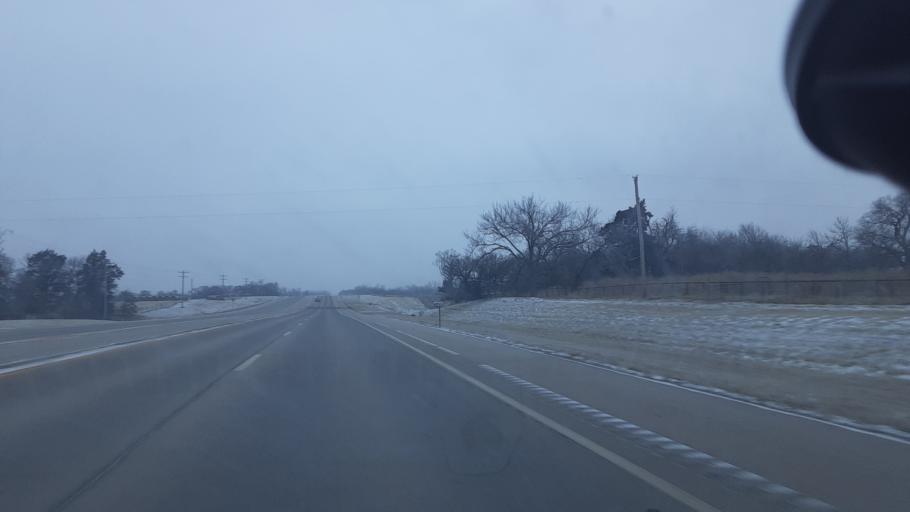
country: US
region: Oklahoma
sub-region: Payne County
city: Perkins
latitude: 35.9855
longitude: -97.0703
